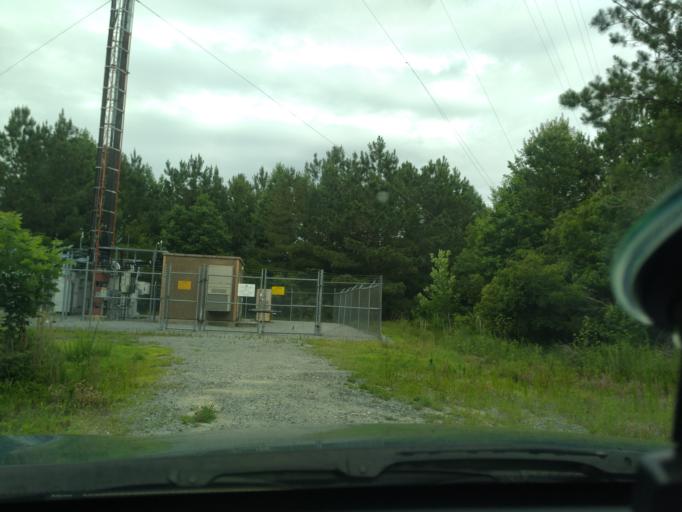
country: US
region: North Carolina
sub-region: Washington County
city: Plymouth
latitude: 35.8715
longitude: -76.7113
